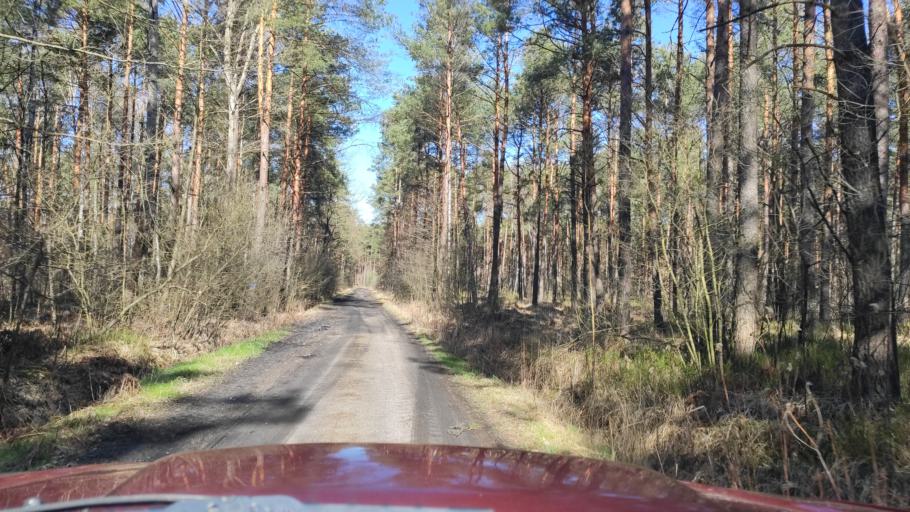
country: PL
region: Masovian Voivodeship
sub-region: Powiat kozienicki
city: Garbatka-Letnisko
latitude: 51.4330
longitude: 21.5472
